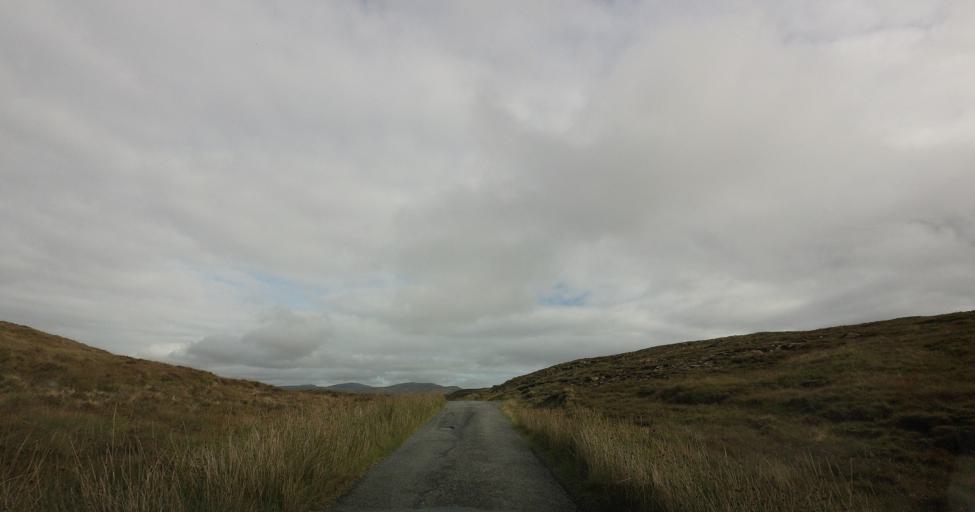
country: GB
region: Scotland
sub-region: Highland
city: Isle of Skye
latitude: 57.4005
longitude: -6.2708
